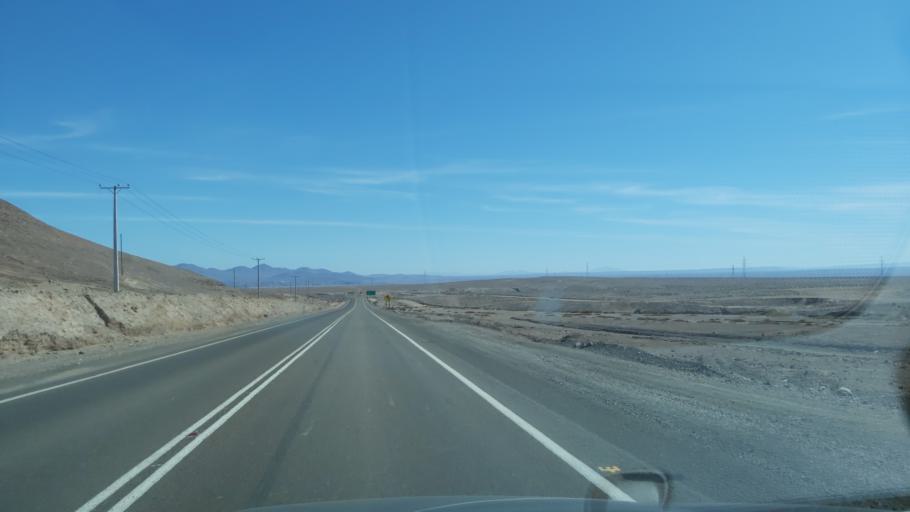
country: CL
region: Atacama
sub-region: Provincia de Chanaral
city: Diego de Almagro
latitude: -26.4571
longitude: -69.9856
